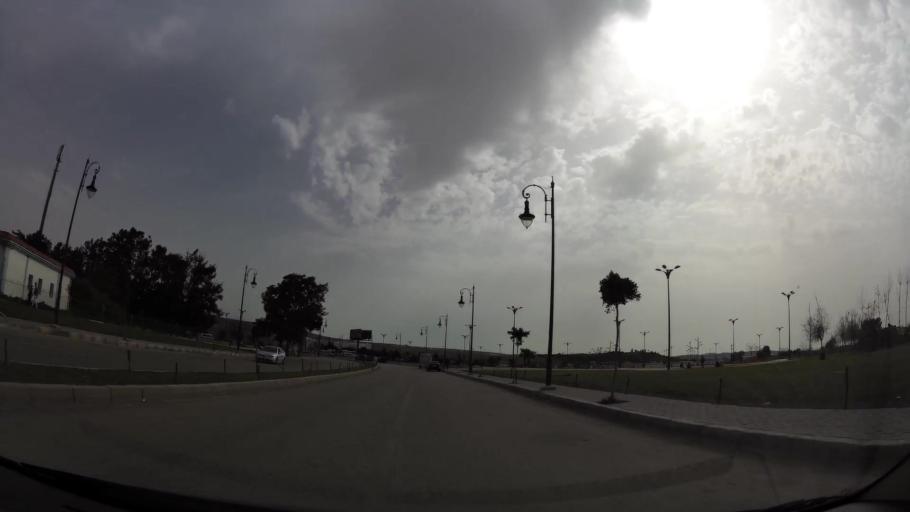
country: MA
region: Tanger-Tetouan
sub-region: Tanger-Assilah
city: Boukhalef
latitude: 35.7313
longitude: -5.8821
